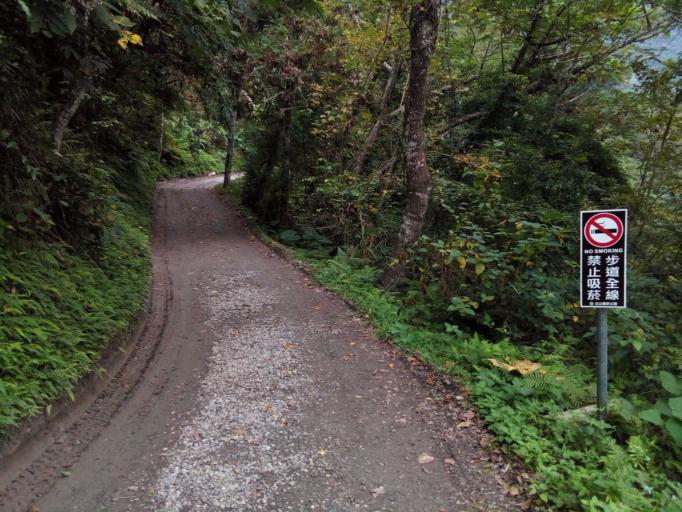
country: TW
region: Taiwan
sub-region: Taitung
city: Taitung
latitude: 23.3287
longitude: 121.2354
